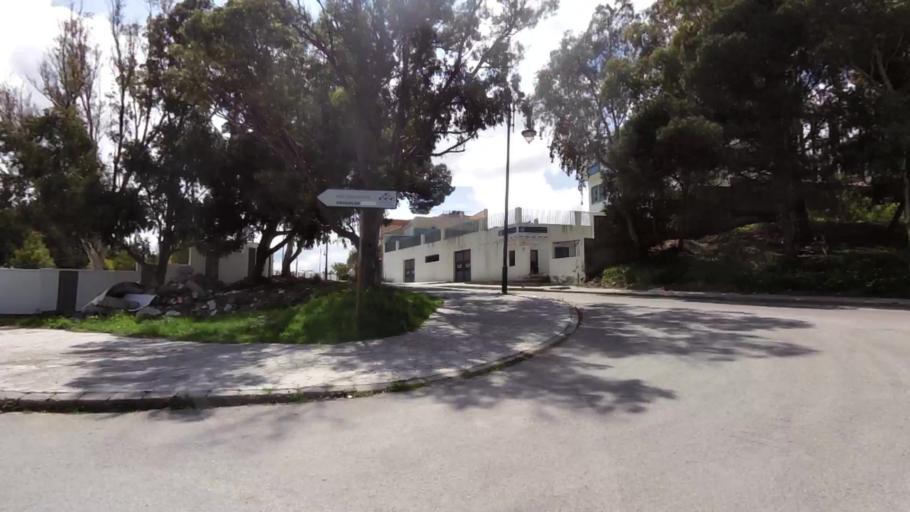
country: MA
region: Tanger-Tetouan
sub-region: Tanger-Assilah
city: Tangier
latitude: 35.7766
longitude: -5.7705
